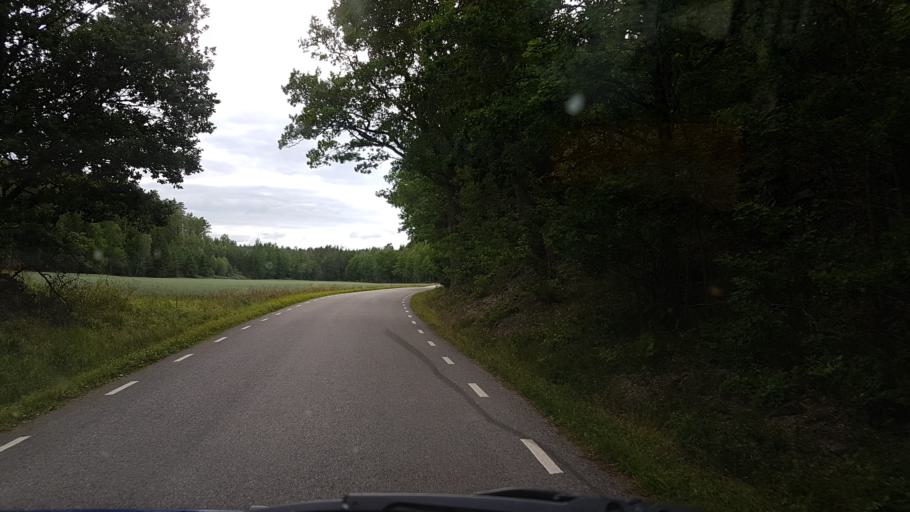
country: SE
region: OEstergoetland
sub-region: Valdemarsviks Kommun
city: Gusum
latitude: 58.4548
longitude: 16.5968
